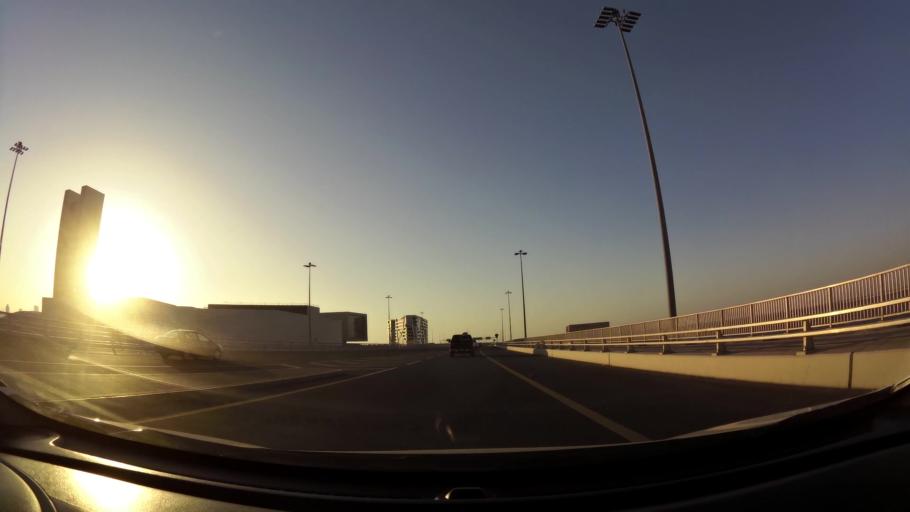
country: BH
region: Muharraq
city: Al Muharraq
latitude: 26.2486
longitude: 50.5882
